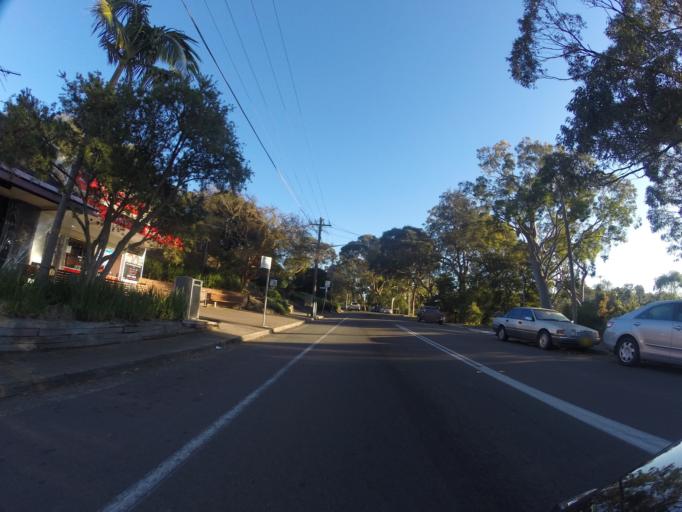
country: AU
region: New South Wales
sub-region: Sutherland Shire
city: Grays Point
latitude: -34.0587
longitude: 151.0815
